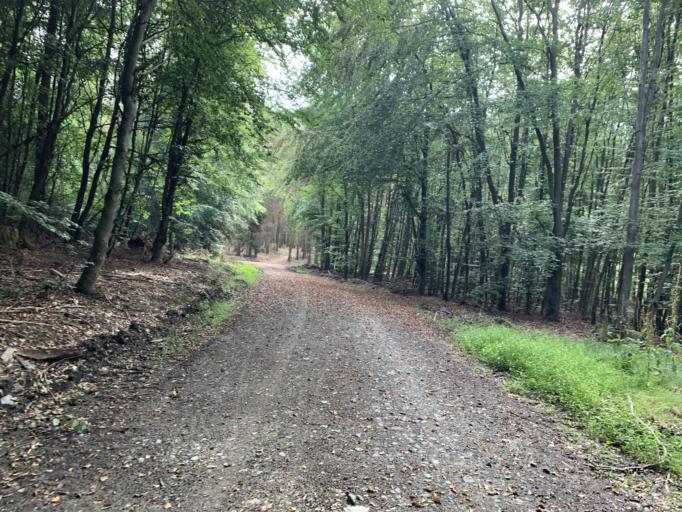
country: DE
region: Rheinland-Pfalz
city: Rettert
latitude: 50.2118
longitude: 7.9394
